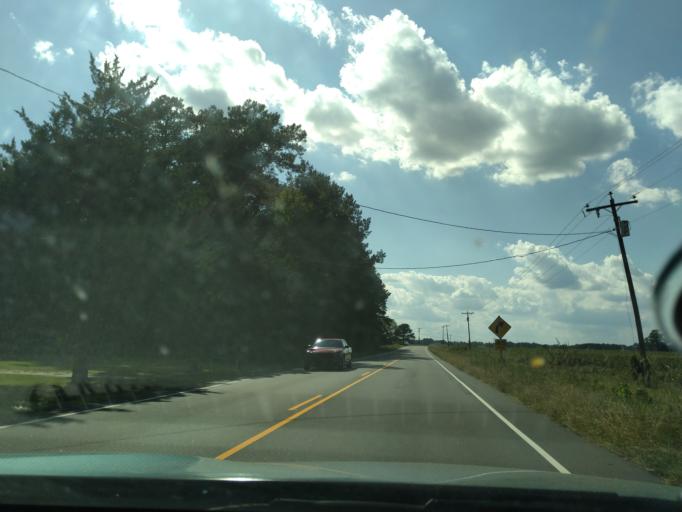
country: US
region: North Carolina
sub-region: Martin County
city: Robersonville
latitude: 35.8224
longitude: -77.2968
